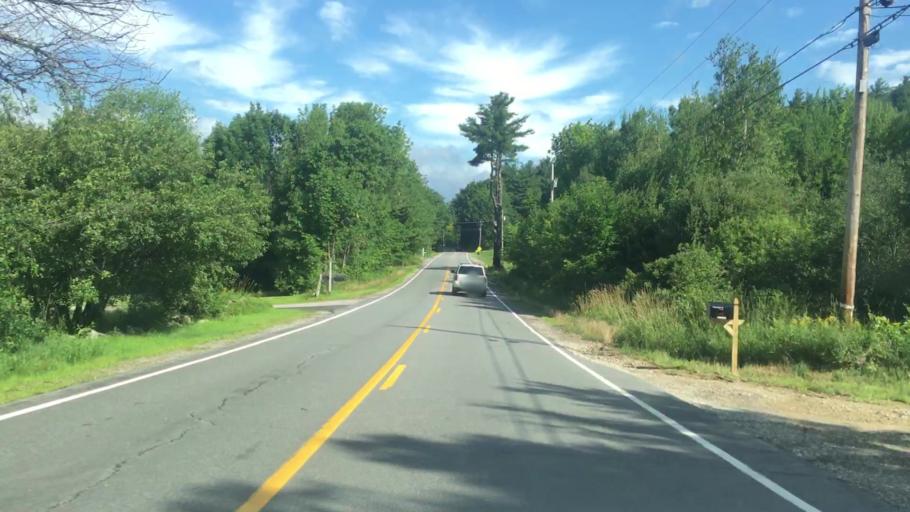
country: US
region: New Hampshire
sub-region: Belknap County
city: Gilford
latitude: 43.5397
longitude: -71.3484
